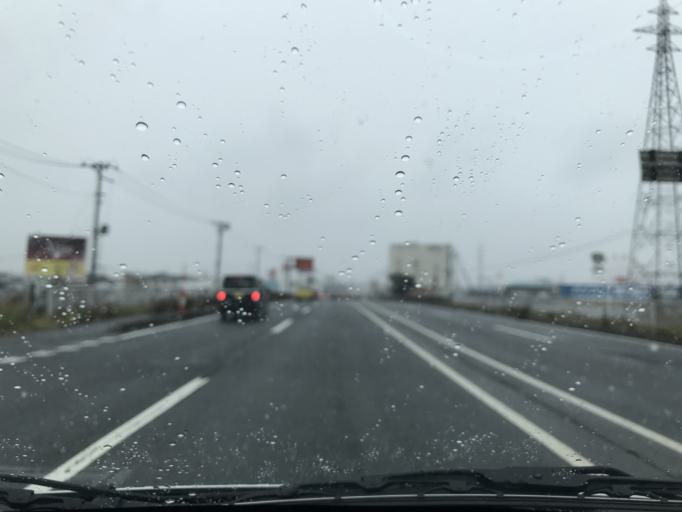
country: JP
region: Iwate
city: Kitakami
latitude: 39.2832
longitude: 141.1028
